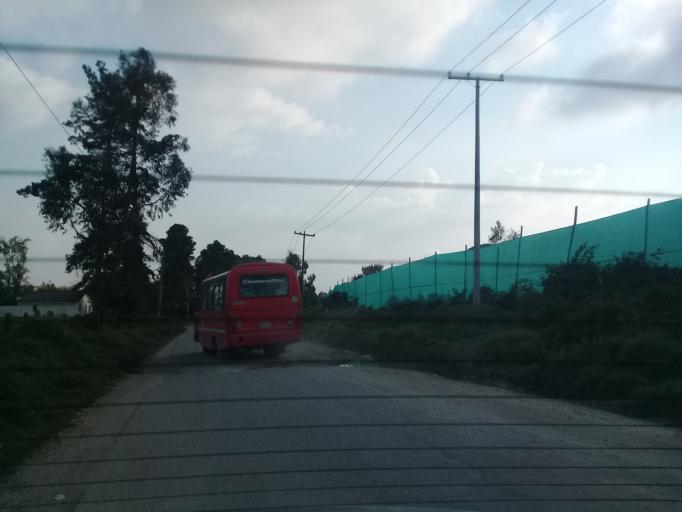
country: CO
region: Cundinamarca
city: Funza
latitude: 4.7801
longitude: -74.2207
